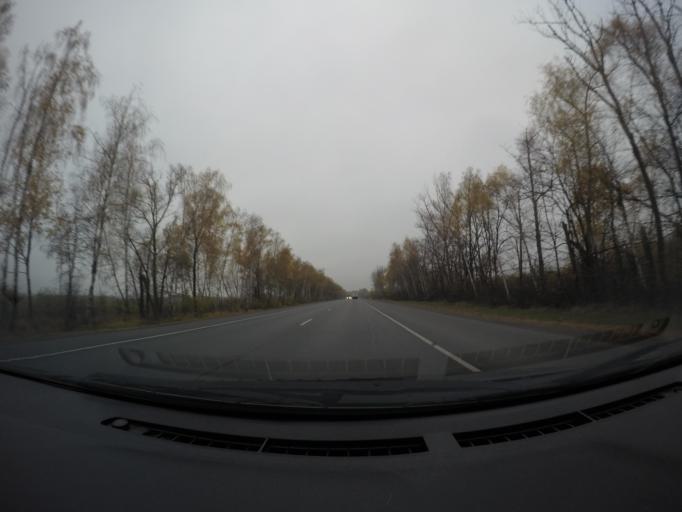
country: RU
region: Moskovskaya
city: Yakovlevskoye
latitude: 55.3644
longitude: 38.0257
